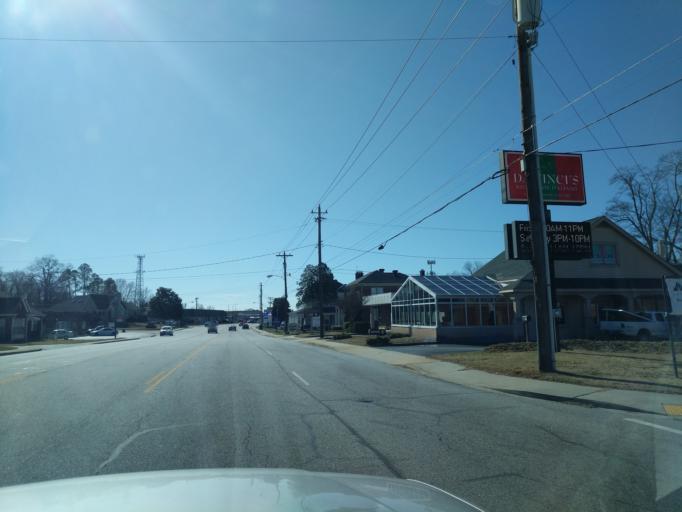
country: US
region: South Carolina
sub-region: Anderson County
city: Anderson
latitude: 34.5130
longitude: -82.6479
